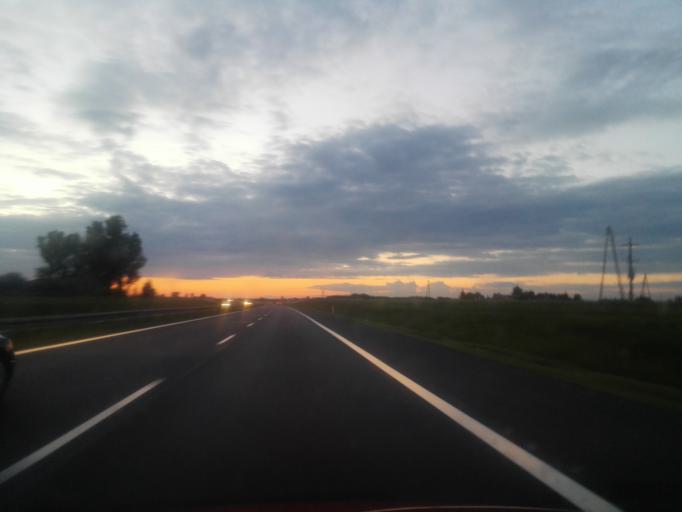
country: PL
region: Lodz Voivodeship
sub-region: Piotrkow Trybunalski
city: Piotrkow Trybunalski
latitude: 51.4662
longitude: 19.6350
